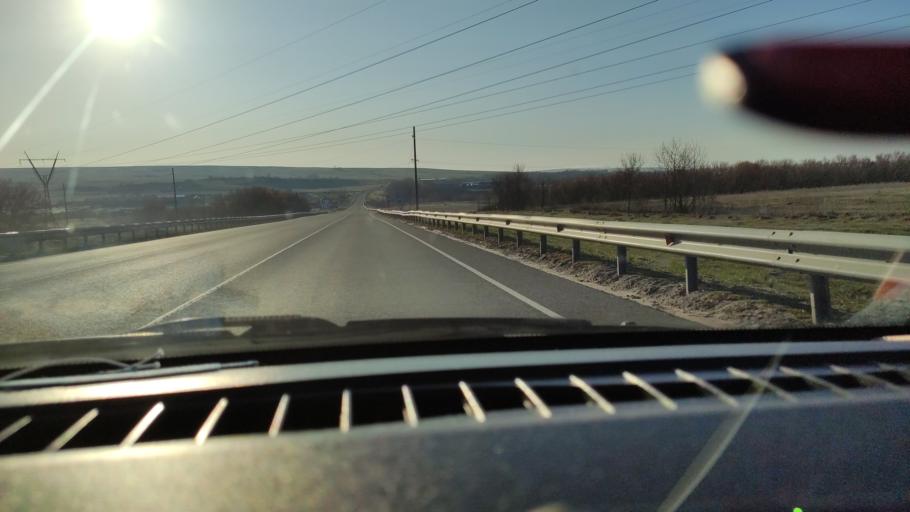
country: RU
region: Saratov
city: Tersa
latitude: 52.0996
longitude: 47.5210
